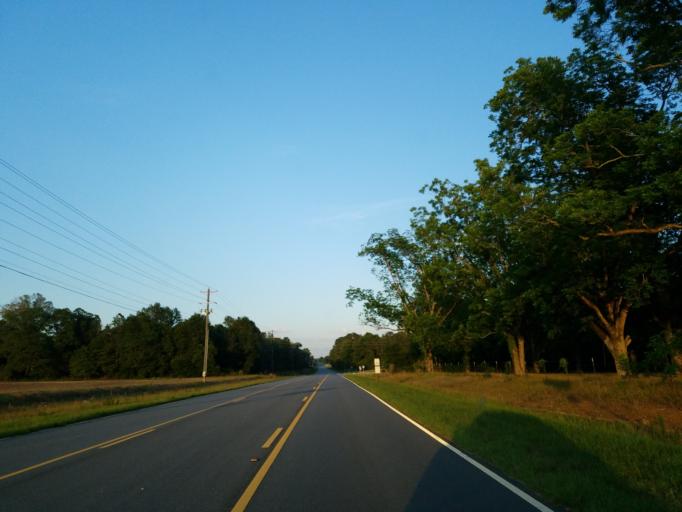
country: US
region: Georgia
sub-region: Crisp County
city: Cordele
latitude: 31.9262
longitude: -83.7583
